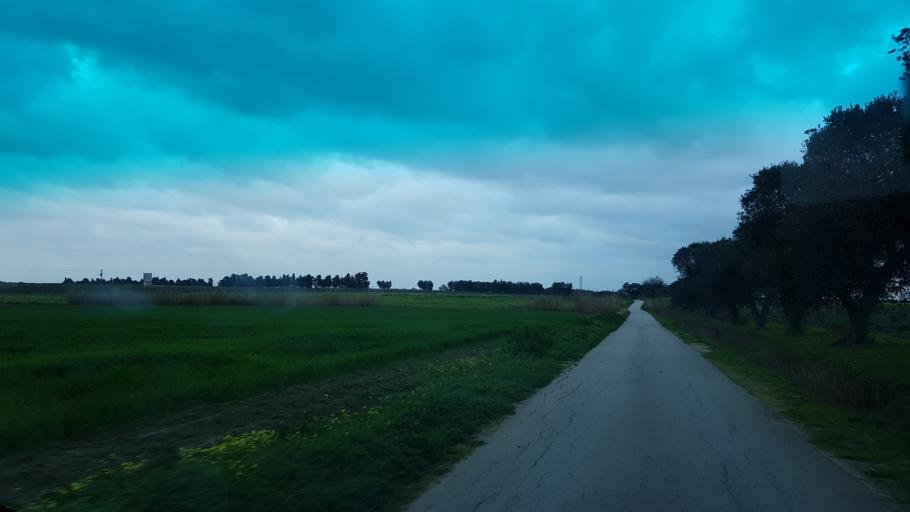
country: IT
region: Apulia
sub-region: Provincia di Brindisi
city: La Rosa
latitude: 40.5946
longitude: 17.9744
